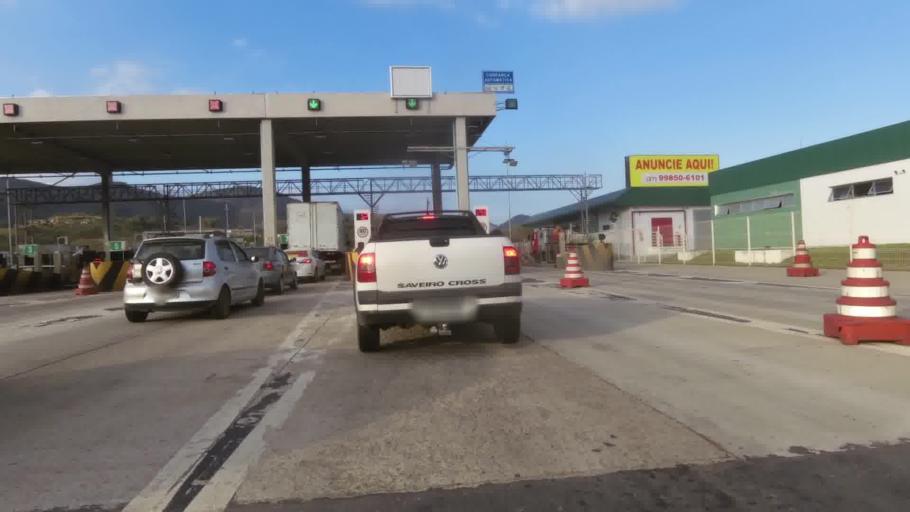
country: BR
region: Espirito Santo
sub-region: Rio Novo Do Sul
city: Rio Novo do Sul
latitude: -20.8788
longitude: -40.9663
